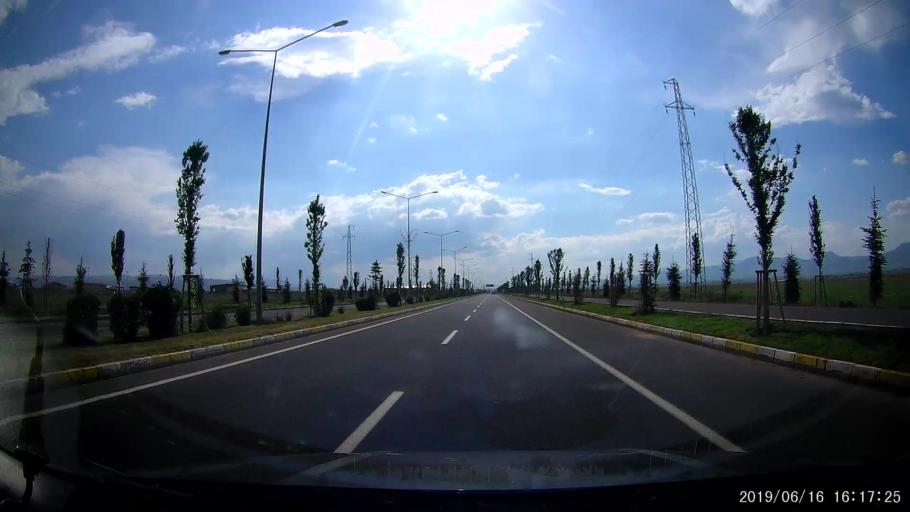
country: TR
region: Erzurum
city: Ilica
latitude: 39.9639
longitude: 41.1872
